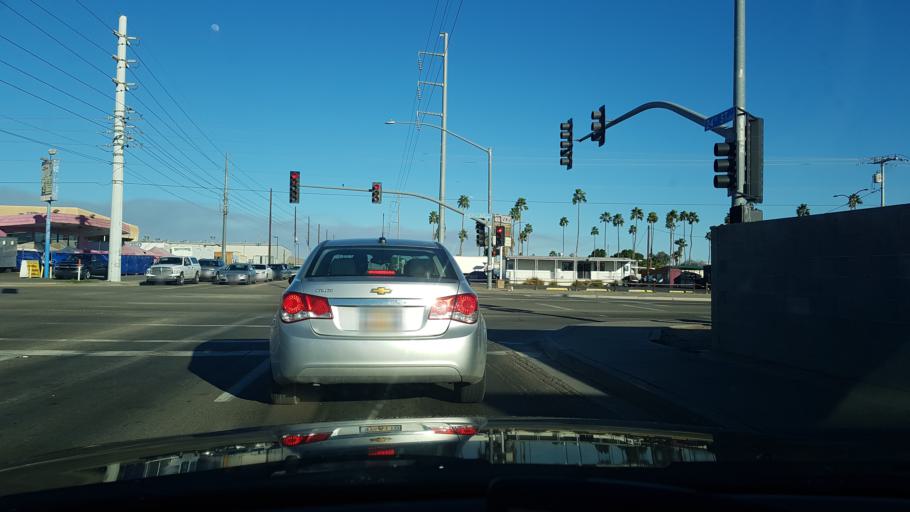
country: US
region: Arizona
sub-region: Yuma County
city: Yuma
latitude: 32.6840
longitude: -114.5991
